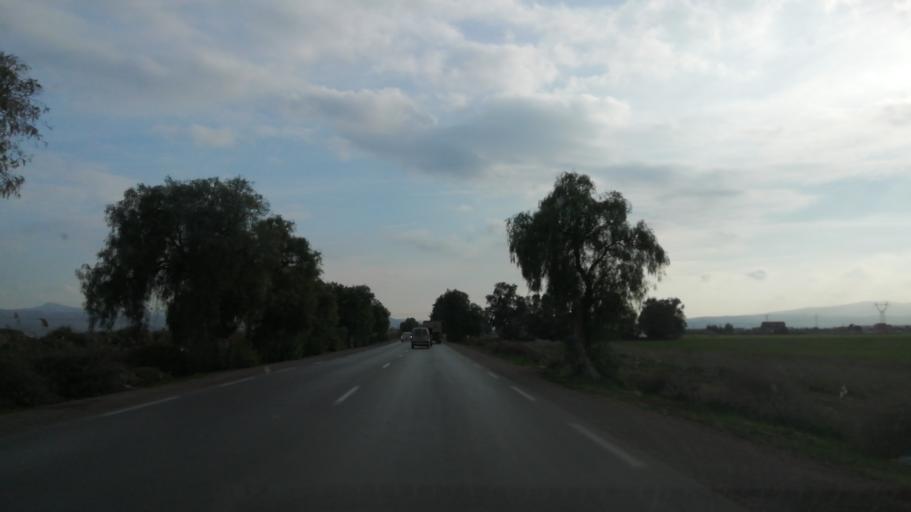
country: DZ
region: Mascara
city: Mascara
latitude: 35.6403
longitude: 0.0604
